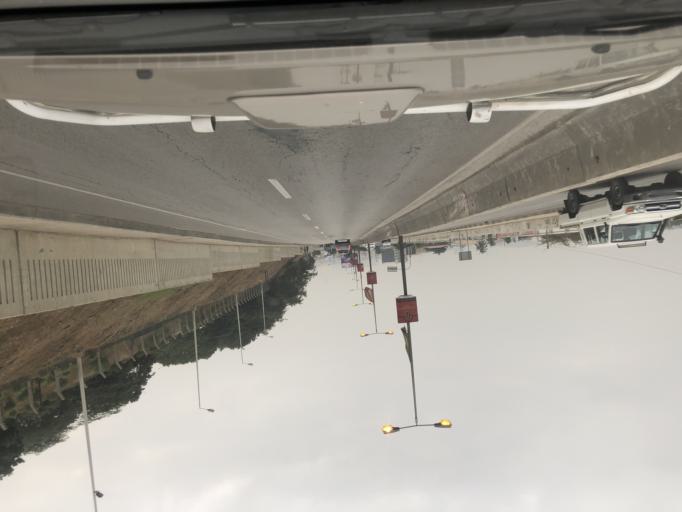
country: AO
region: Luanda
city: Luanda
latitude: -8.8632
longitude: 13.2024
